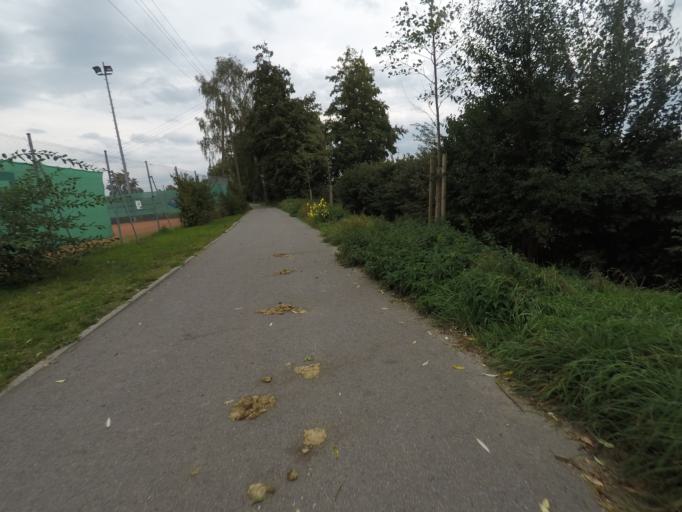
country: DE
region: Baden-Wuerttemberg
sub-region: Regierungsbezirk Stuttgart
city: Herrenberg
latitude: 48.5703
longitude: 8.8825
